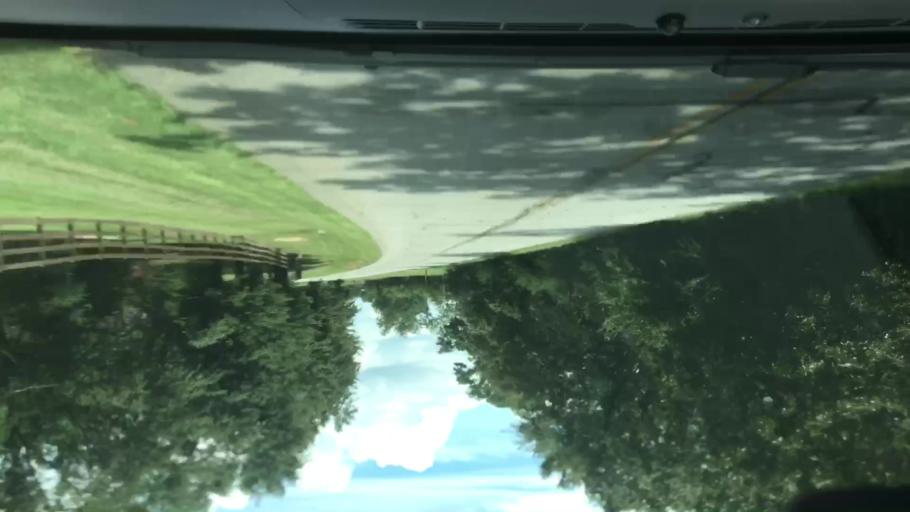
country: US
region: Georgia
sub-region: Stewart County
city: Lumpkin
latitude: 32.1366
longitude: -84.9997
